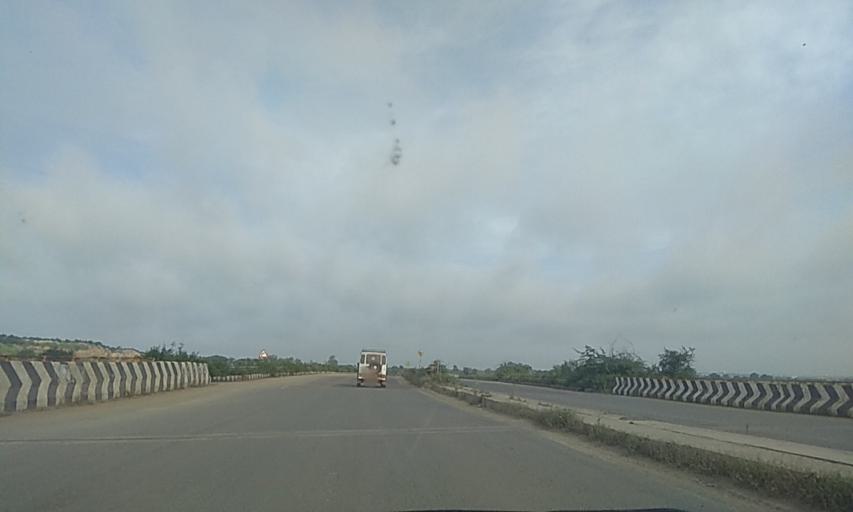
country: IN
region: Karnataka
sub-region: Haveri
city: Haveri
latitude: 14.7627
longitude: 75.4335
